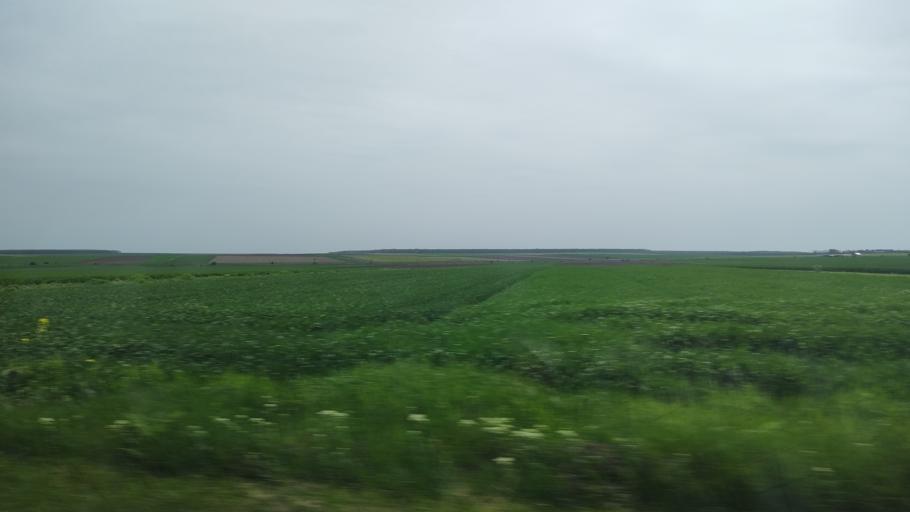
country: RO
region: Constanta
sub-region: Comuna Cobadin
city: Cobadin
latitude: 44.0766
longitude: 28.2409
